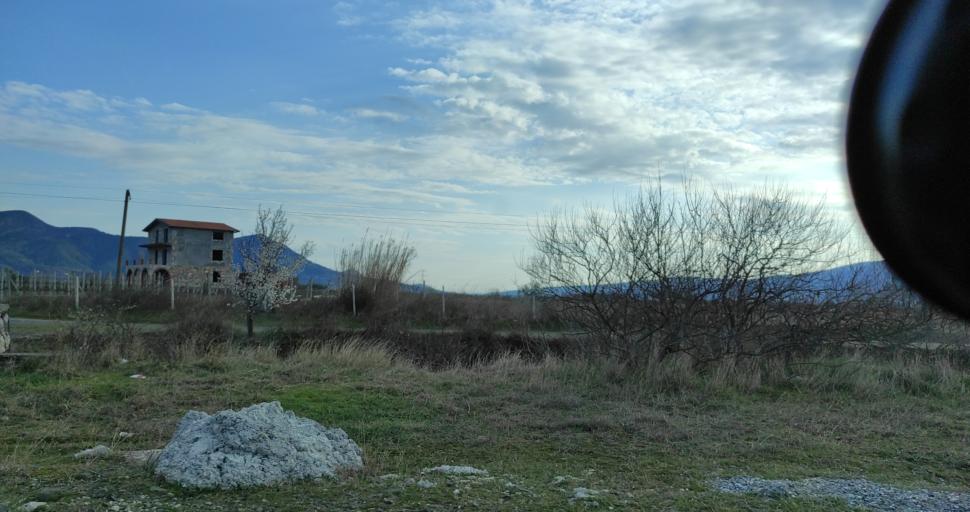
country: AL
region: Lezhe
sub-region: Rrethi i Lezhes
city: Kallmeti i Madh
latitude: 41.8784
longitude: 19.6721
